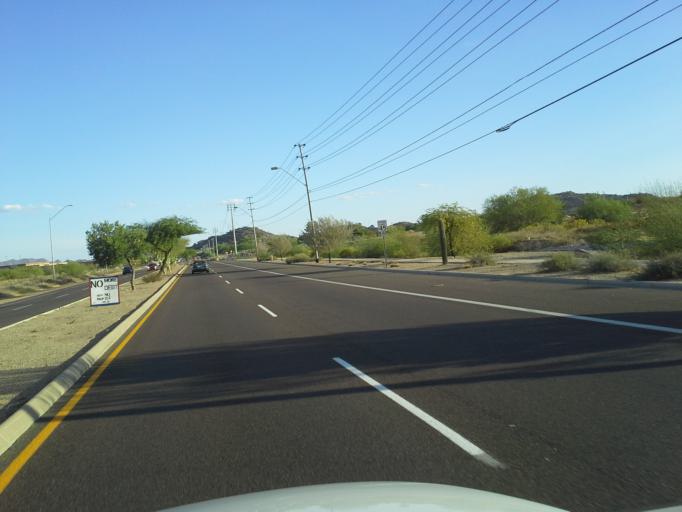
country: US
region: Arizona
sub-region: Maricopa County
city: Cave Creek
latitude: 33.6835
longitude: -112.0312
